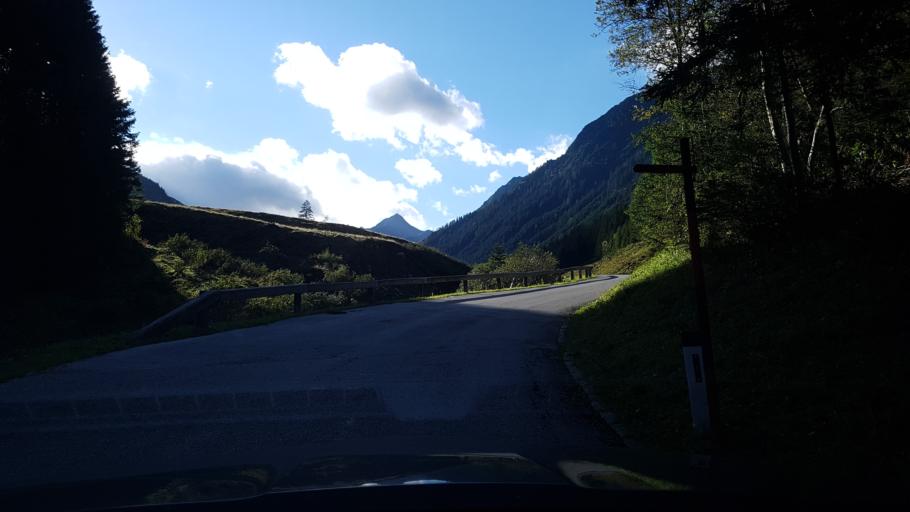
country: AT
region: Styria
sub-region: Politischer Bezirk Liezen
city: Sankt Nikolai im Solktal
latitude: 47.3125
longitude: 14.0571
